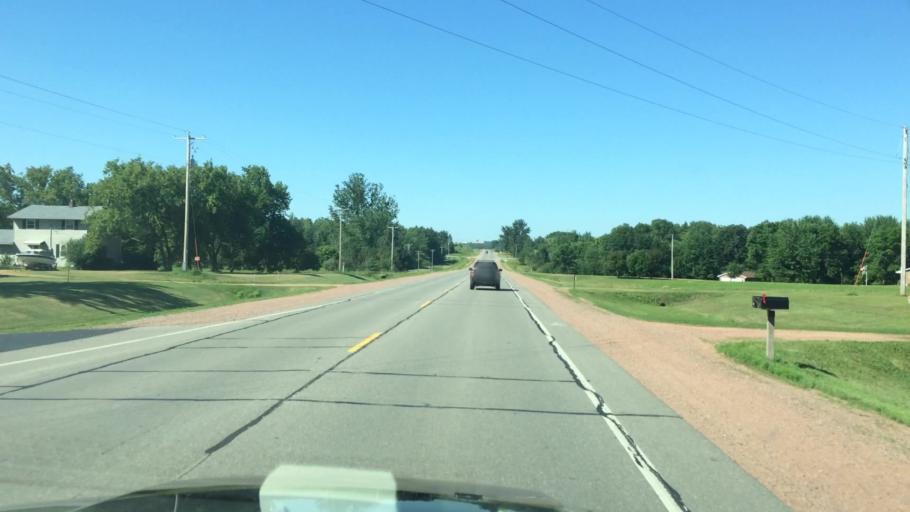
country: US
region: Wisconsin
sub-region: Wood County
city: Marshfield
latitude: 44.7139
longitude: -90.1142
